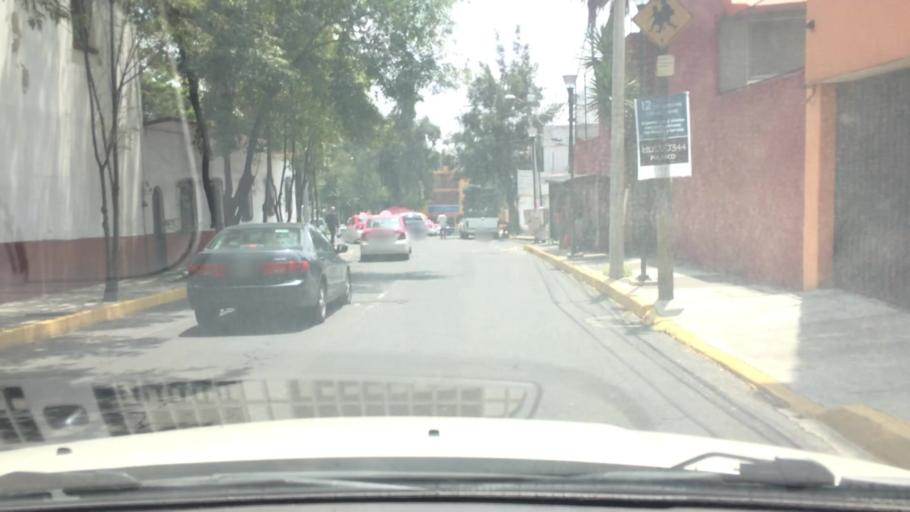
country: MX
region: Mexico City
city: Alvaro Obregon
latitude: 19.3580
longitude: -99.2102
